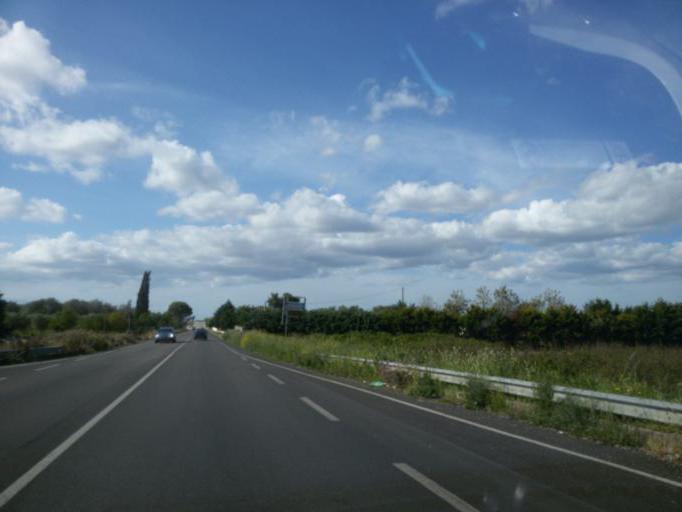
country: IT
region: Apulia
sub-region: Provincia di Brindisi
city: Mesagne
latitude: 40.5631
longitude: 17.7875
